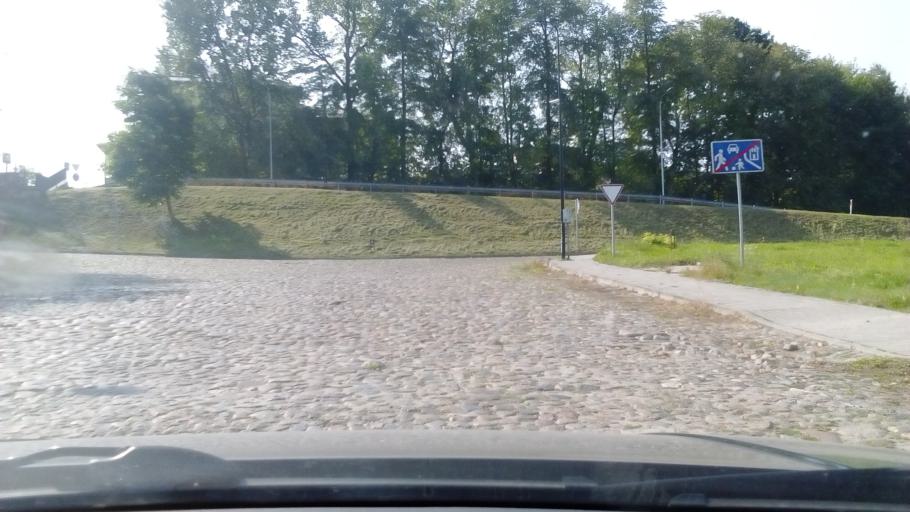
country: LT
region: Alytaus apskritis
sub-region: Alytus
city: Alytus
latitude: 54.4012
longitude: 24.0499
